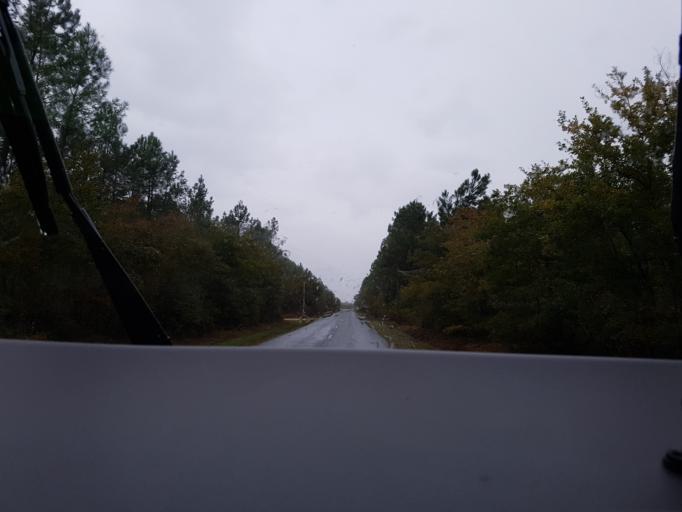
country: FR
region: Aquitaine
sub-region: Departement de la Gironde
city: Saint-Symphorien
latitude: 44.3353
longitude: -0.5977
